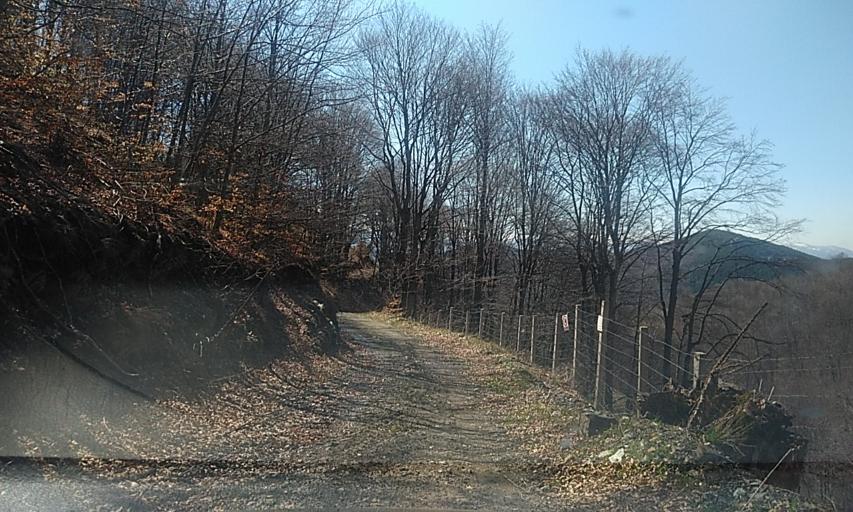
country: RS
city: Radovnica
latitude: 42.3515
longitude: 22.3385
